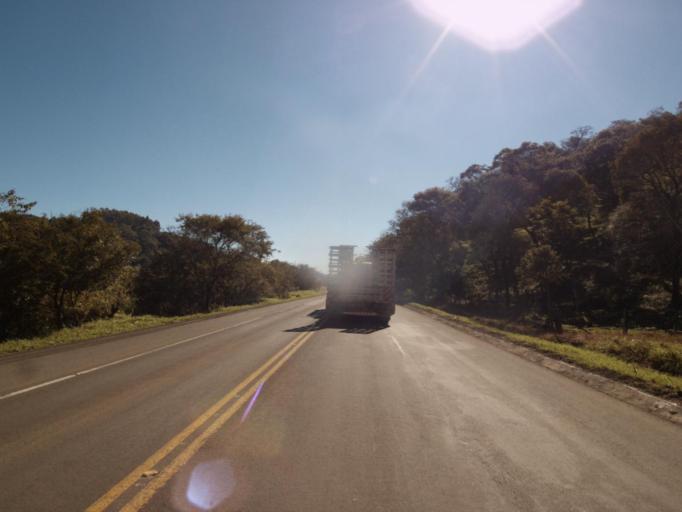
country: BR
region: Rio Grande do Sul
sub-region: Frederico Westphalen
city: Frederico Westphalen
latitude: -26.8179
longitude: -53.4287
